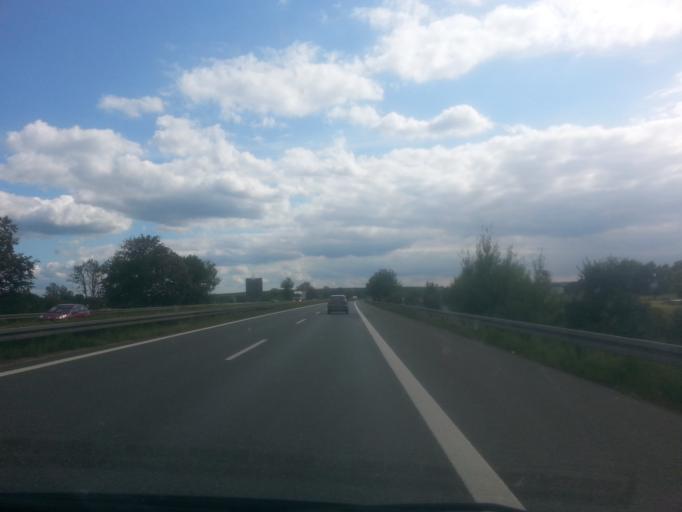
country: DE
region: Bavaria
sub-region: Upper Palatinate
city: Schwarzenfeld
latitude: 49.3797
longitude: 12.1498
